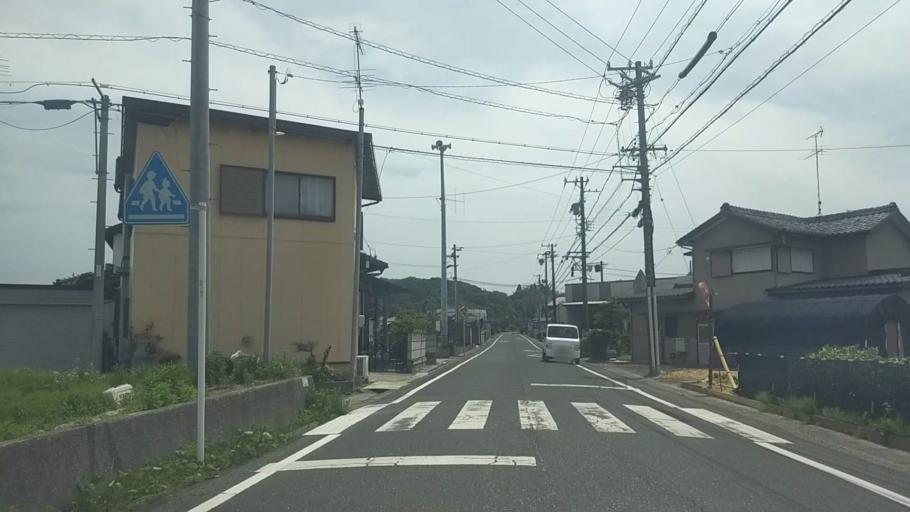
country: JP
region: Shizuoka
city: Kosai-shi
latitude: 34.7468
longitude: 137.5313
